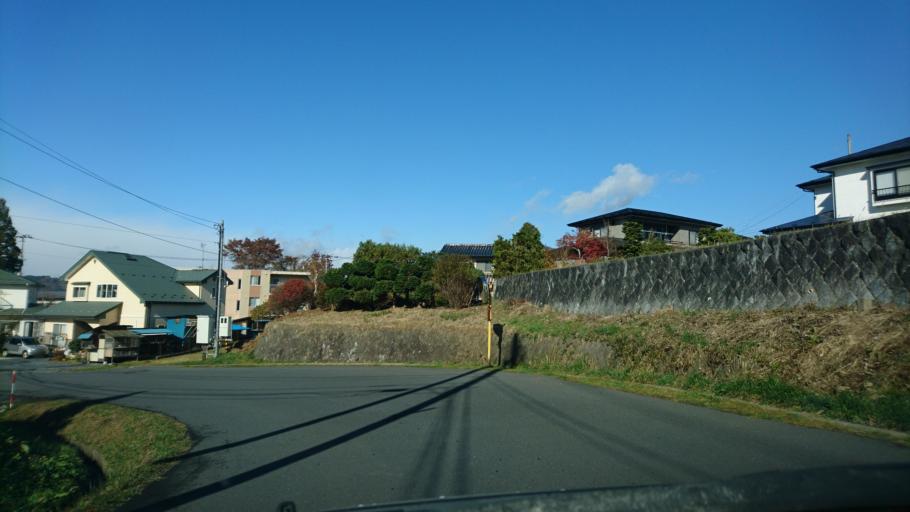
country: JP
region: Iwate
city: Ichinoseki
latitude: 38.9221
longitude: 141.1213
